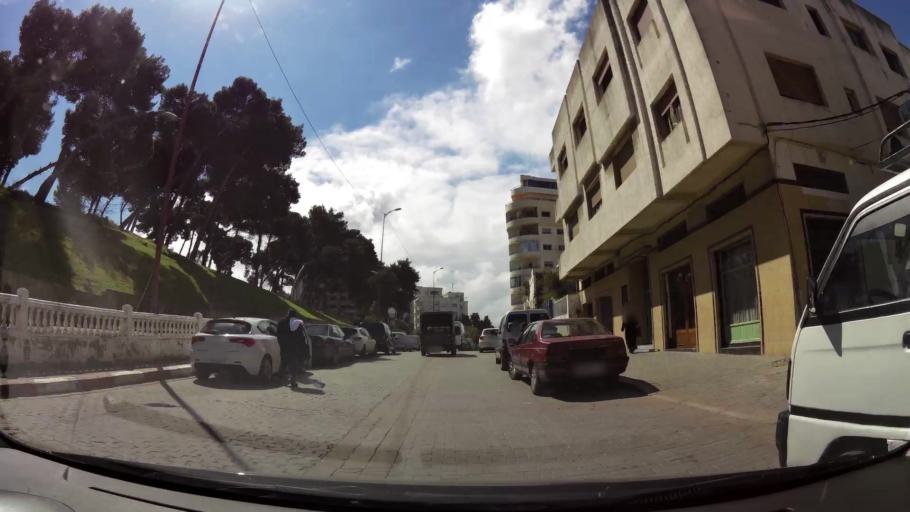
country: MA
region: Tanger-Tetouan
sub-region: Tanger-Assilah
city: Tangier
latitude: 35.7844
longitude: -5.8180
